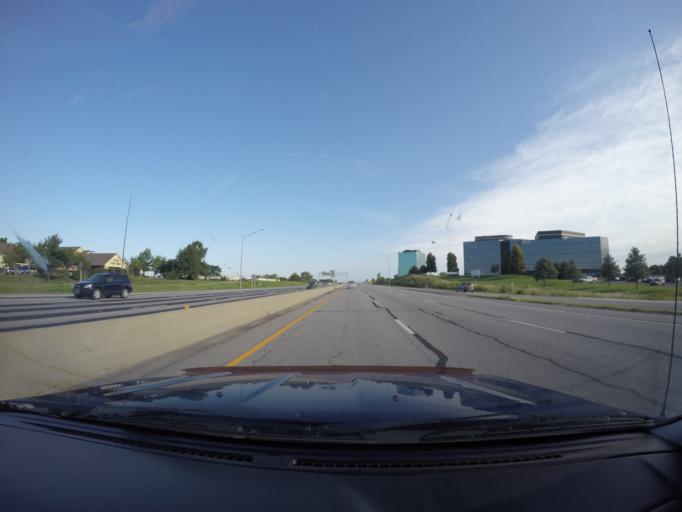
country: US
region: Missouri
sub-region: Platte County
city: Weatherby Lake
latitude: 39.2755
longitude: -94.6709
